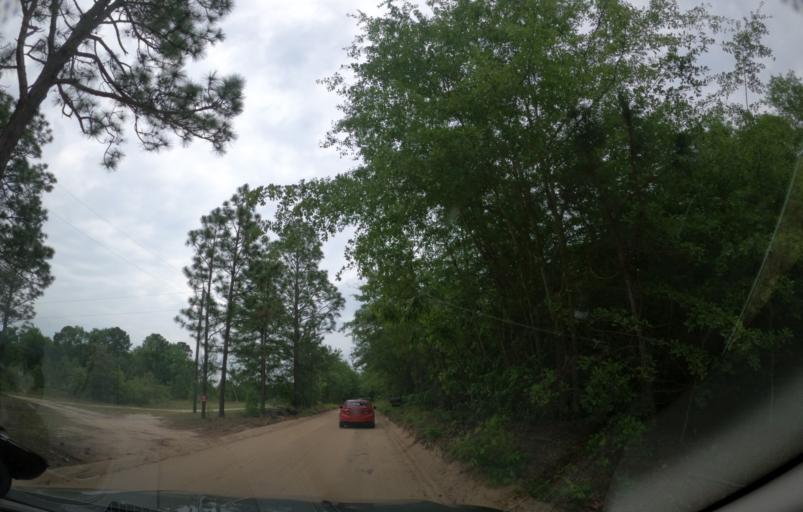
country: US
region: South Carolina
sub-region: Lexington County
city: Gaston
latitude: 33.6480
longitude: -81.2565
